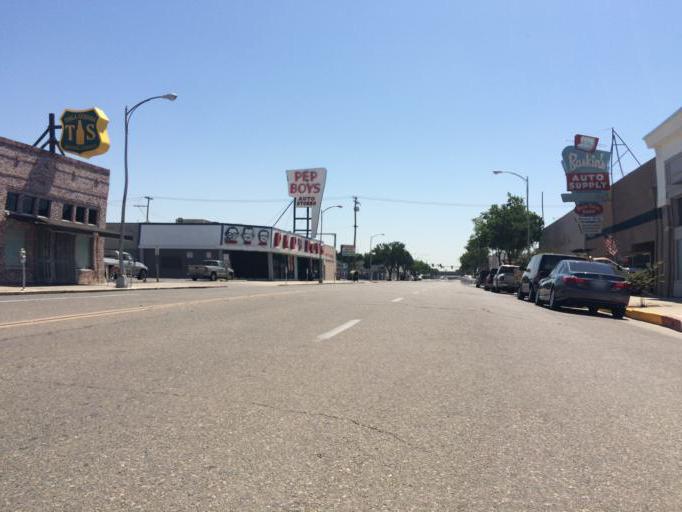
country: US
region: California
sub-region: Fresno County
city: Fresno
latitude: 36.7310
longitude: -119.7888
